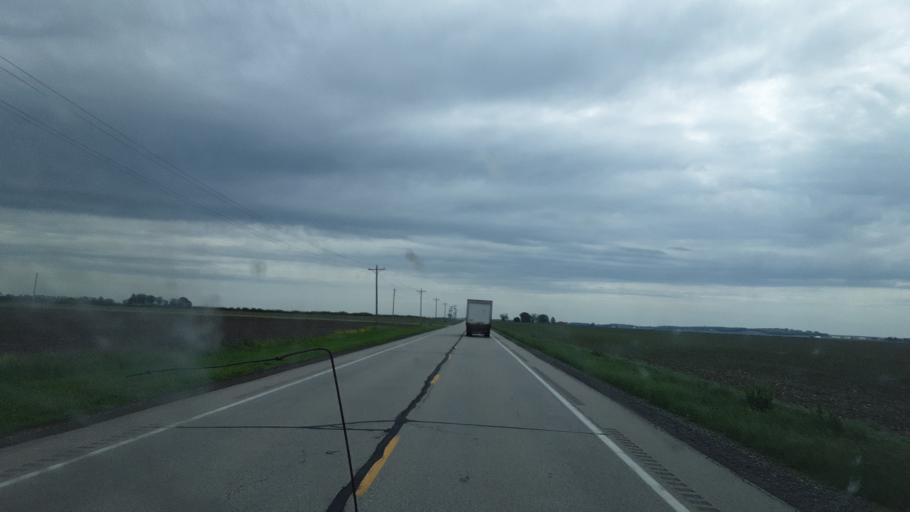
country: US
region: Illinois
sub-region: Mason County
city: Mason City
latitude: 40.3042
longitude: -89.7454
